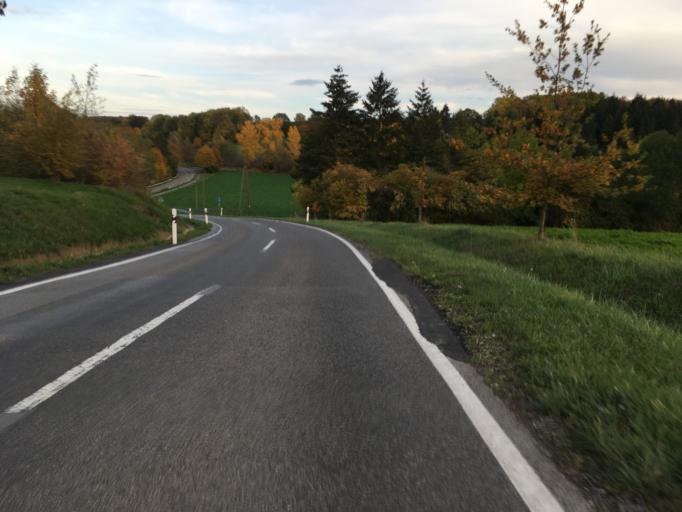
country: DE
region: Baden-Wuerttemberg
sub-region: Regierungsbezirk Stuttgart
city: Kirchardt
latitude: 49.2424
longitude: 8.9629
